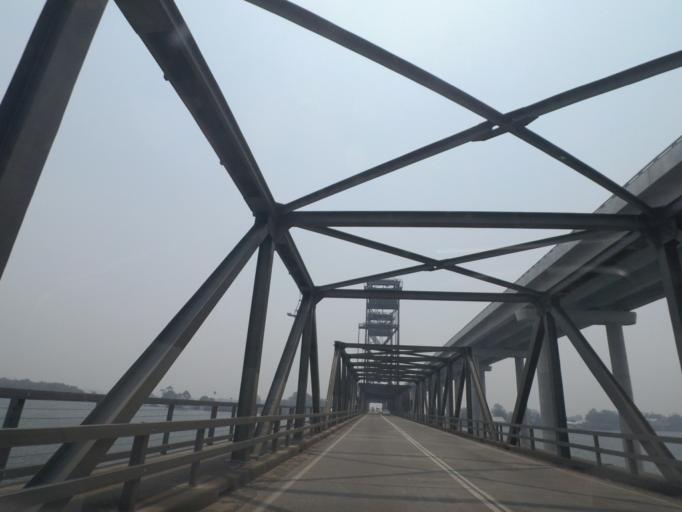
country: AU
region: New South Wales
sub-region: Clarence Valley
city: Maclean
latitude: -29.4313
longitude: 153.2409
